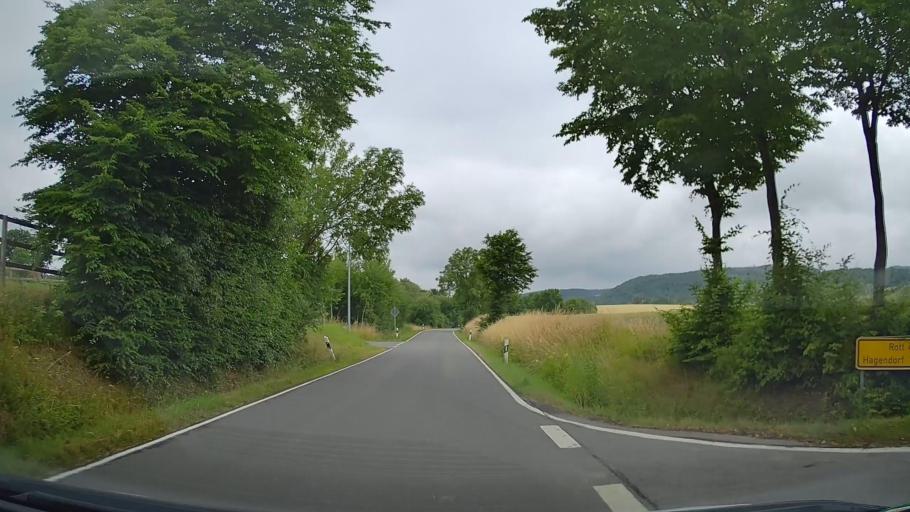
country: DE
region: Lower Saxony
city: Rinteln
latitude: 52.1081
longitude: 9.1218
